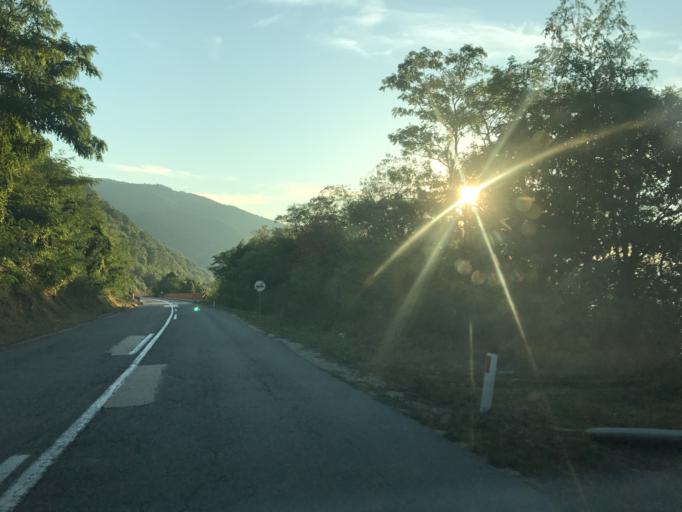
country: RO
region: Caras-Severin
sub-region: Comuna Berzasca
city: Berzasca
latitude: 44.6306
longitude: 21.9725
